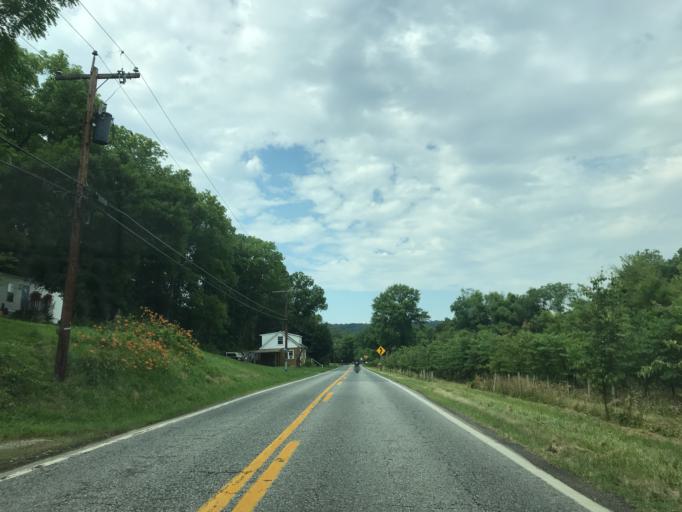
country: US
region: Maryland
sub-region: Harford County
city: Bel Air North
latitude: 39.6181
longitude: -76.4004
